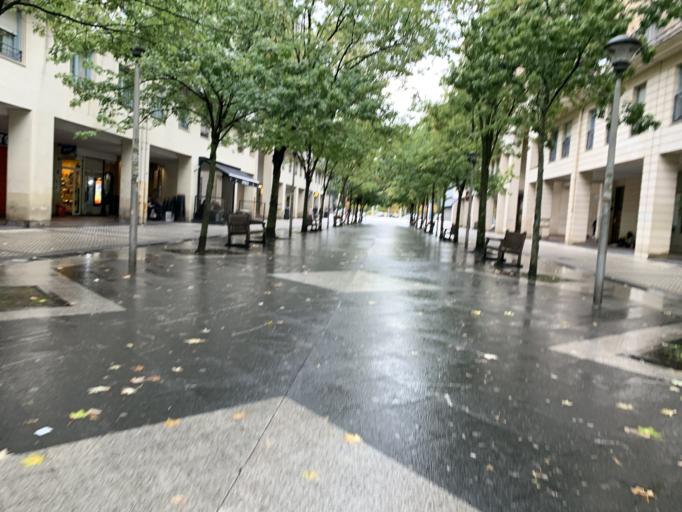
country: ES
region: Basque Country
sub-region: Provincia de Guipuzcoa
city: San Sebastian
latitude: 43.3102
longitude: -2.0072
